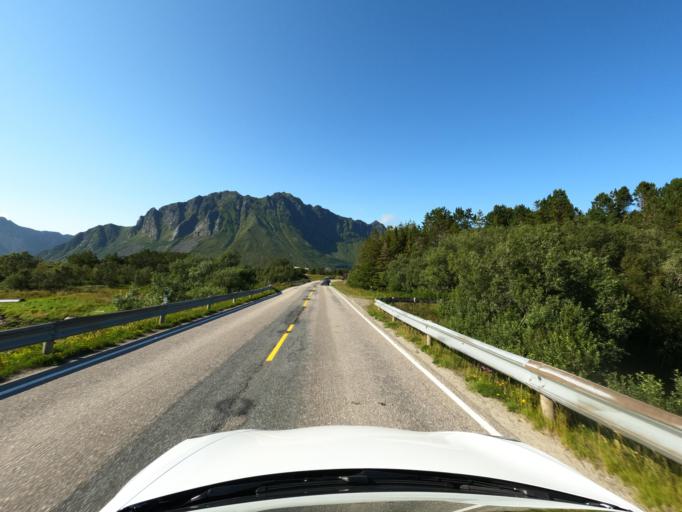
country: NO
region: Nordland
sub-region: Vagan
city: Kabelvag
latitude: 68.2515
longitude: 14.2776
